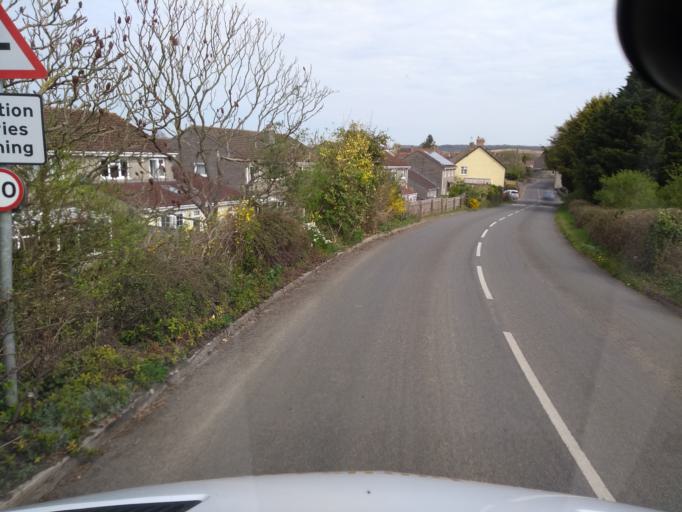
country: GB
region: England
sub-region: Somerset
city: Ilchester
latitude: 51.0499
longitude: -2.7399
